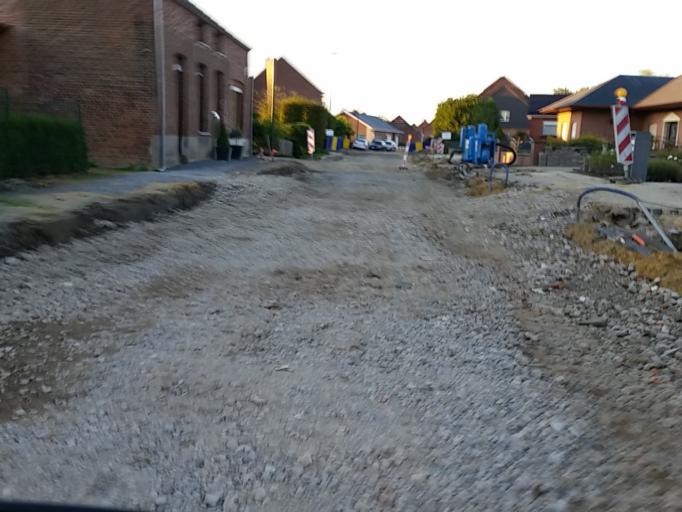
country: BE
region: Flanders
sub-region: Provincie Vlaams-Brabant
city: Kampenhout
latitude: 50.9507
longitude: 4.5453
